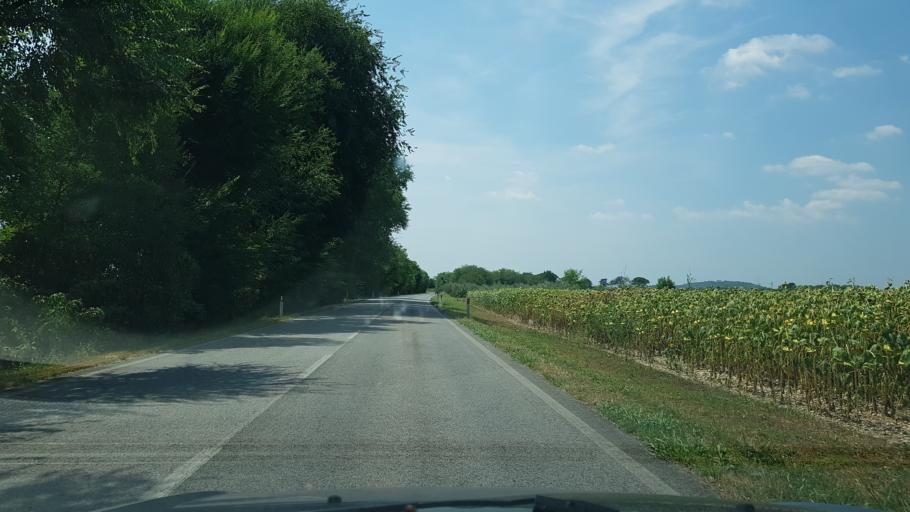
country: IT
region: Friuli Venezia Giulia
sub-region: Provincia di Gorizia
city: Moraro
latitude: 45.9232
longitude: 13.4947
